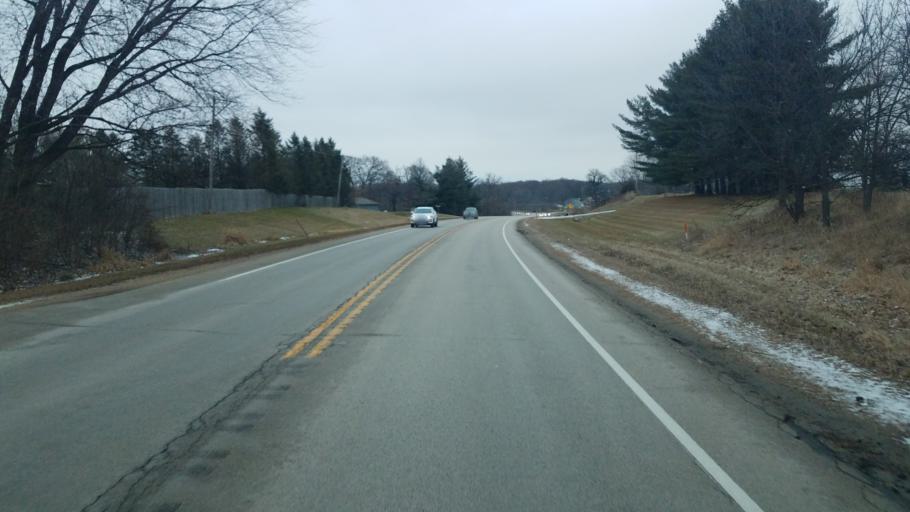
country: US
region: Illinois
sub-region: Kane County
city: Elburn
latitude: 41.8270
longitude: -88.4671
